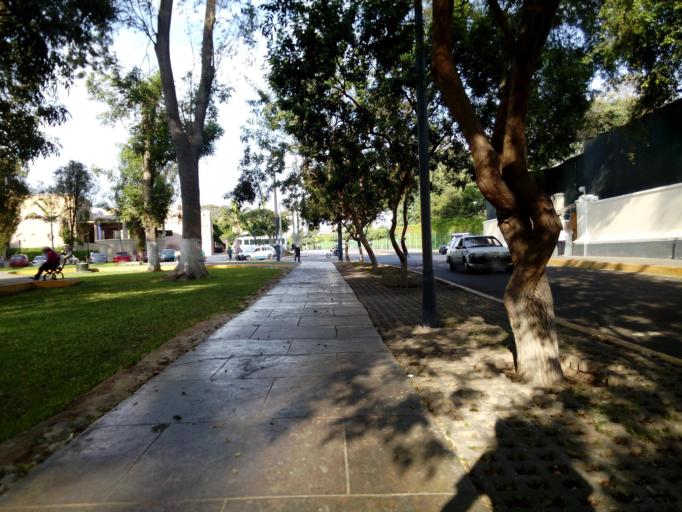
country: PE
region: Lima
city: Lima
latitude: -12.0697
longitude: -77.0361
